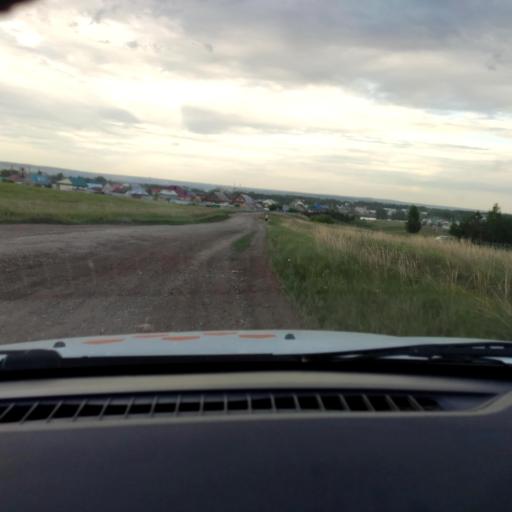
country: RU
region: Bashkortostan
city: Chishmy
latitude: 54.6107
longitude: 55.3951
